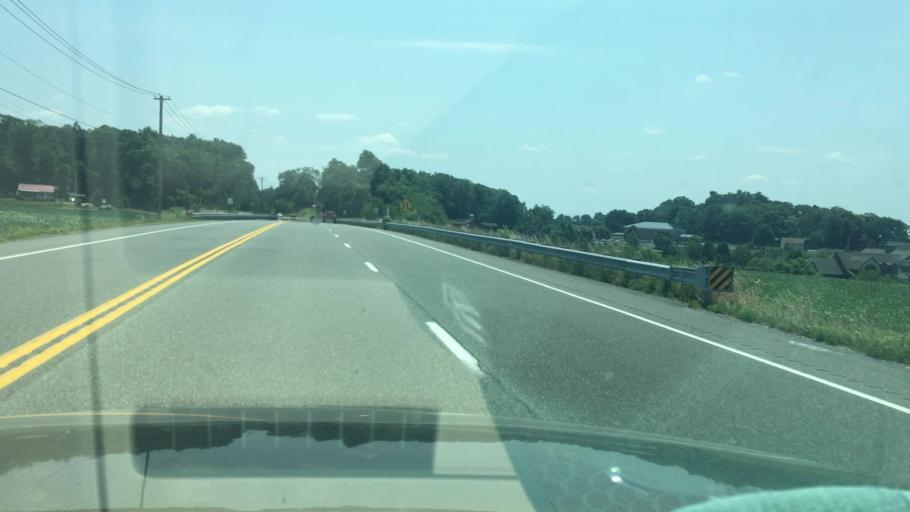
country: US
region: Pennsylvania
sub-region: Lehigh County
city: Schnecksville
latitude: 40.6188
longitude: -75.6604
